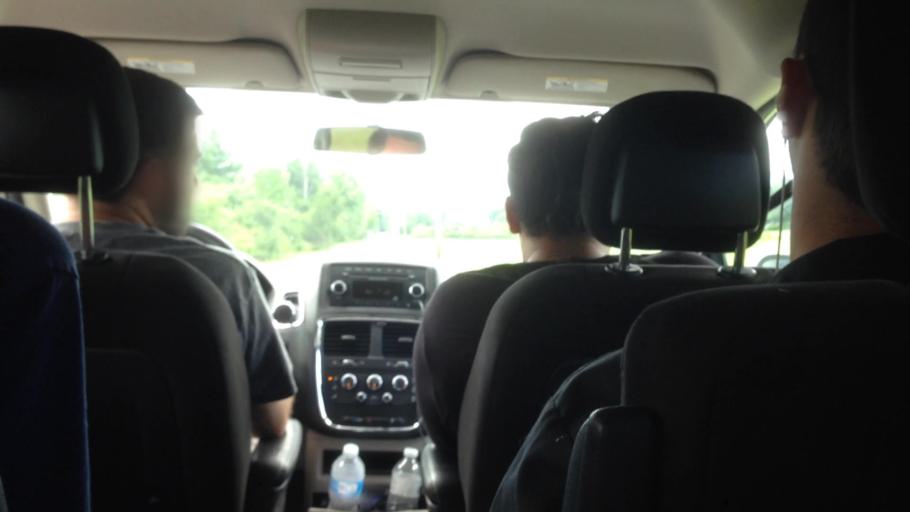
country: US
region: New York
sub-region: Dutchess County
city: Tivoli
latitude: 42.0472
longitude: -73.8988
